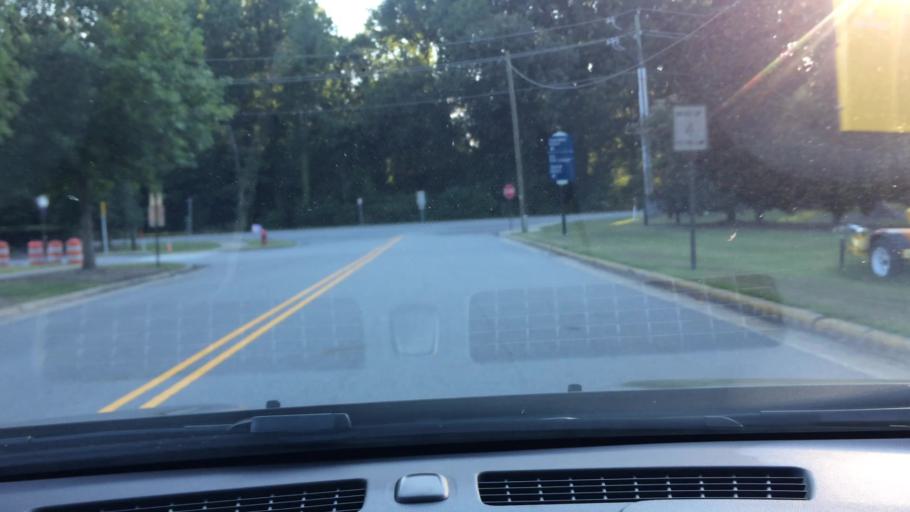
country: US
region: North Carolina
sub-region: Pitt County
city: Greenville
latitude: 35.5987
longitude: -77.3697
